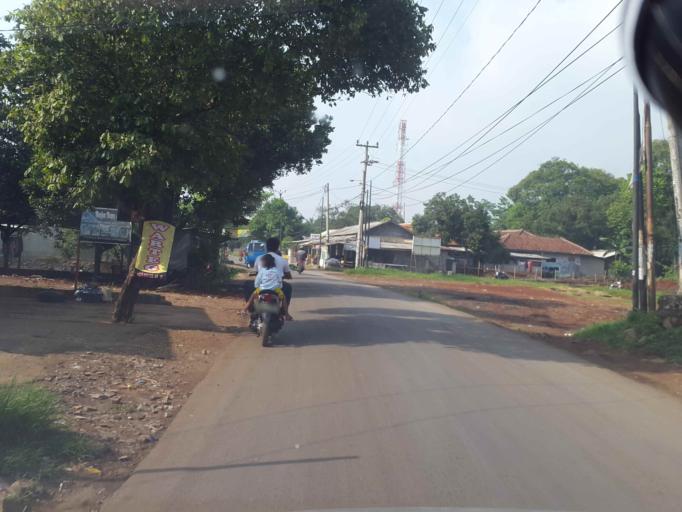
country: ID
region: West Java
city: Cileungsir
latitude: -6.3835
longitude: 106.9879
